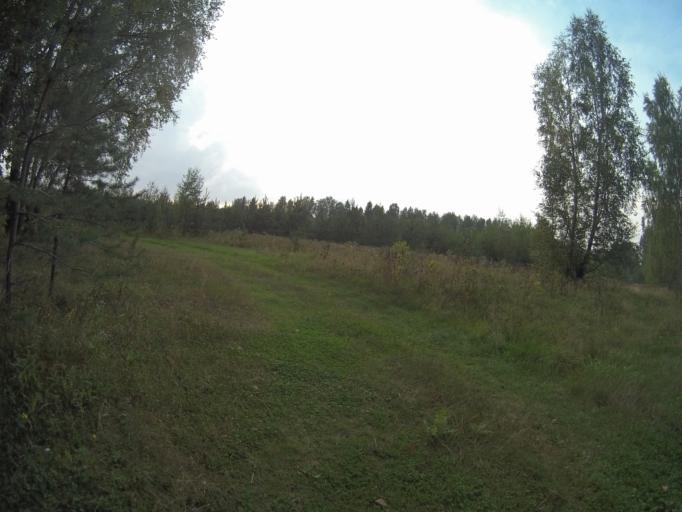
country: RU
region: Vladimir
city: Raduzhnyy
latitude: 55.9912
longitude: 40.2685
